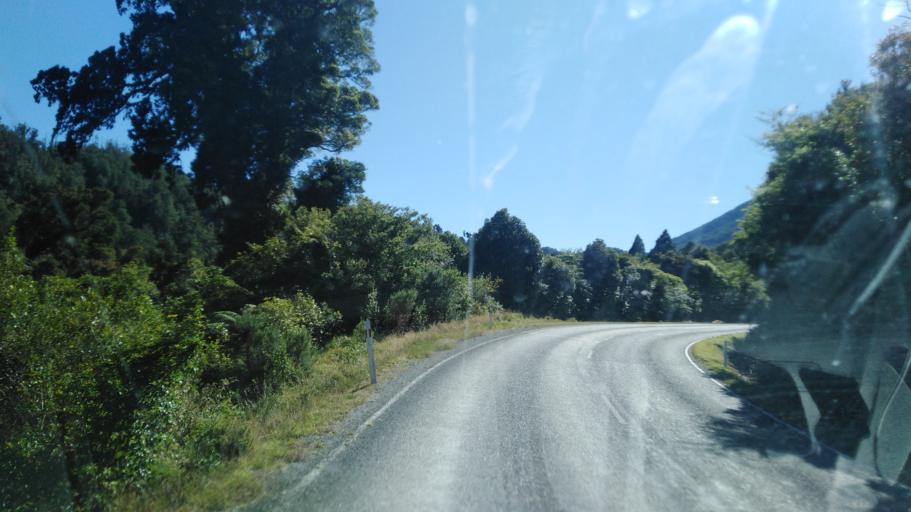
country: NZ
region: West Coast
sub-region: Buller District
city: Westport
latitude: -41.5290
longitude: 171.9956
